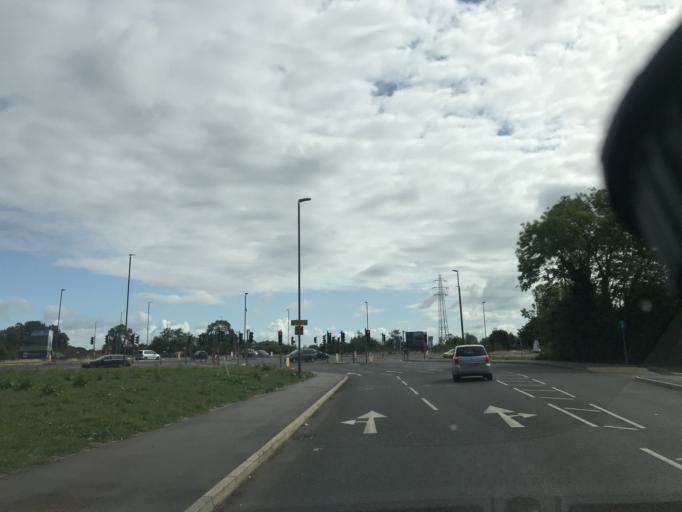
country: GB
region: England
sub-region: Buckinghamshire
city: Aylesbury
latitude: 51.8210
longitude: -0.7922
